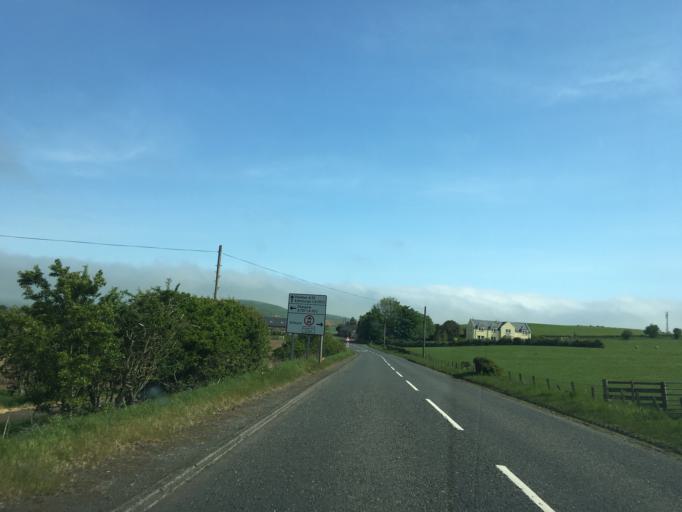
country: GB
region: Scotland
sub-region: The Scottish Borders
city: West Linton
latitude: 55.6828
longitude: -3.3999
